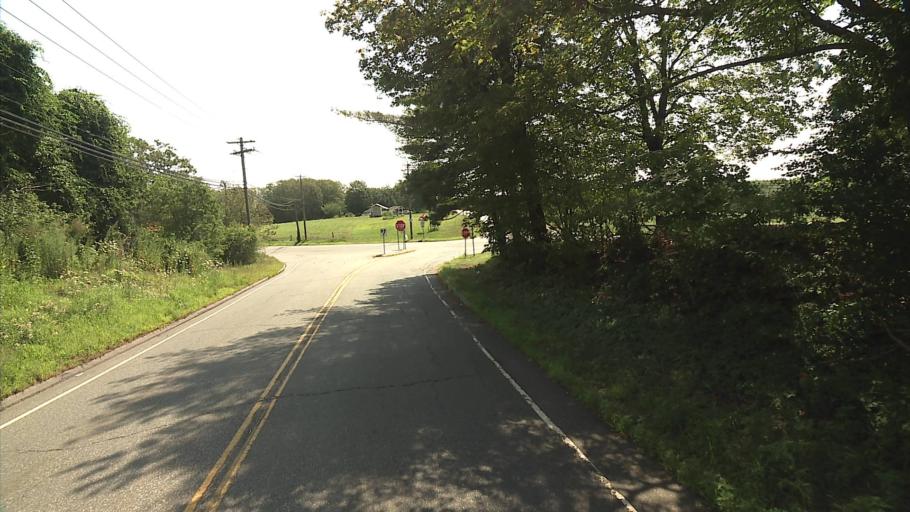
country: US
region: Connecticut
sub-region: New London County
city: Montville Center
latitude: 41.4982
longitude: -72.2245
